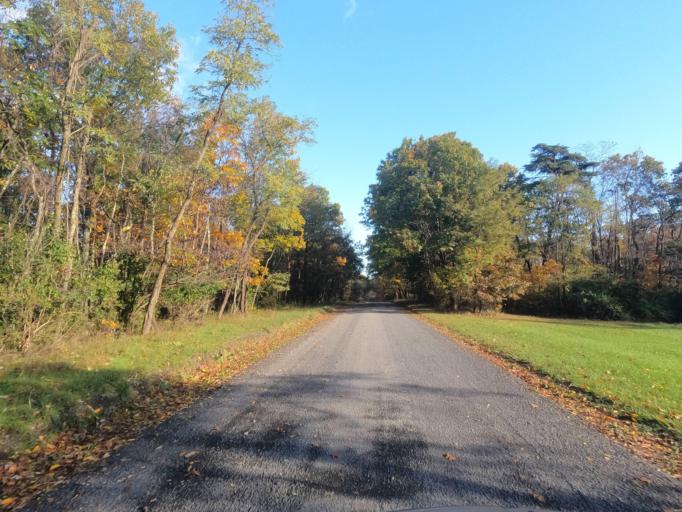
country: US
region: West Virginia
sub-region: Morgan County
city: Berkeley Springs
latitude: 39.6190
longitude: -78.4884
